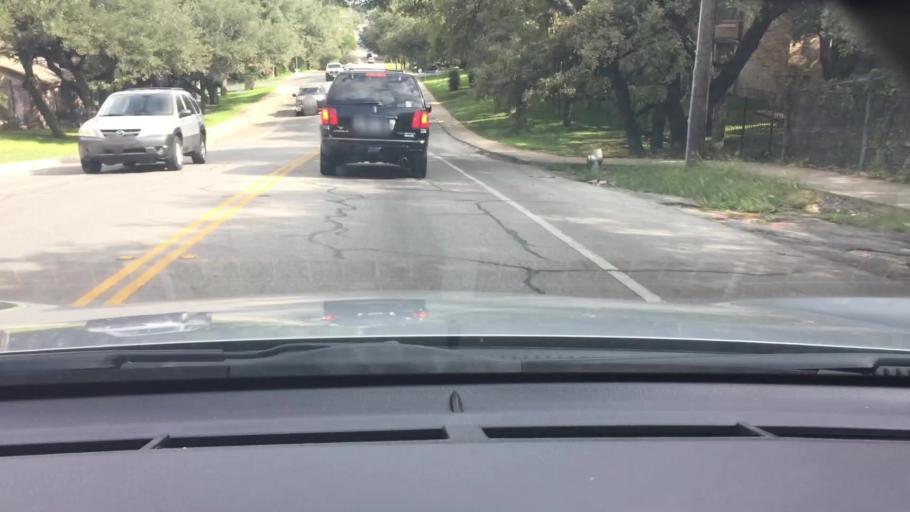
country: US
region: Texas
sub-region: Bexar County
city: Shavano Park
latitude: 29.5506
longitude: -98.5691
